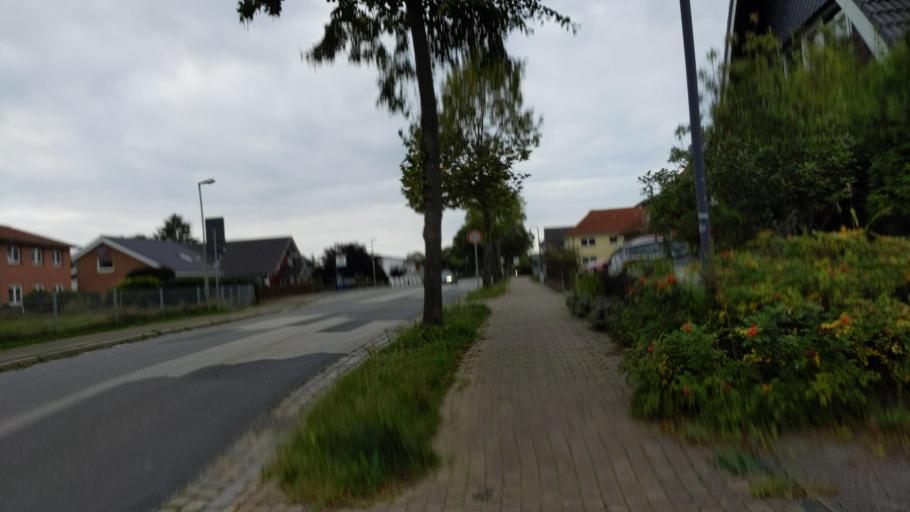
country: DE
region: Schleswig-Holstein
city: Krummesse
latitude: 53.7833
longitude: 10.6409
